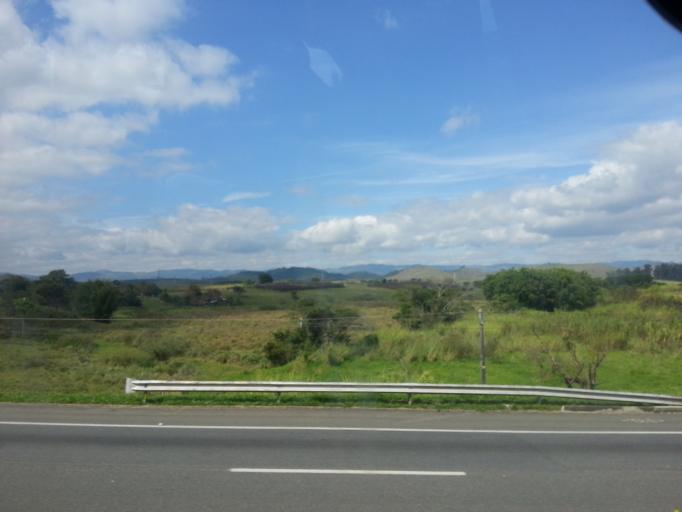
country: BR
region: Sao Paulo
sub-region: Lorena
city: Lorena
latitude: -22.7314
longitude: -45.0779
